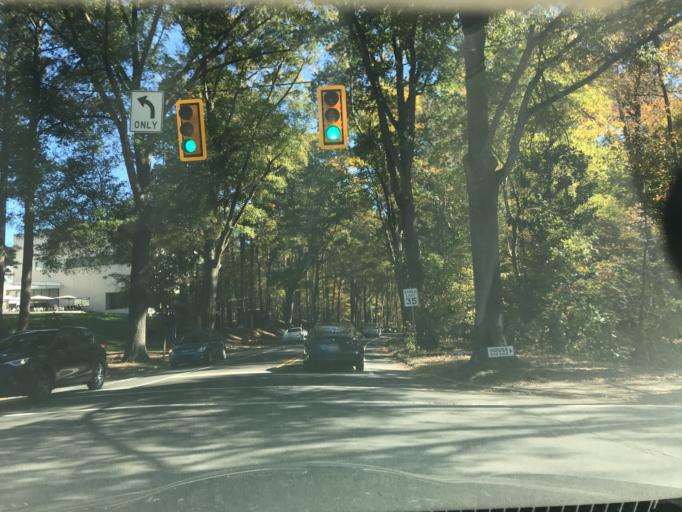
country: US
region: North Carolina
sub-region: Durham County
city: Durham
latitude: 35.9984
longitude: -78.9304
